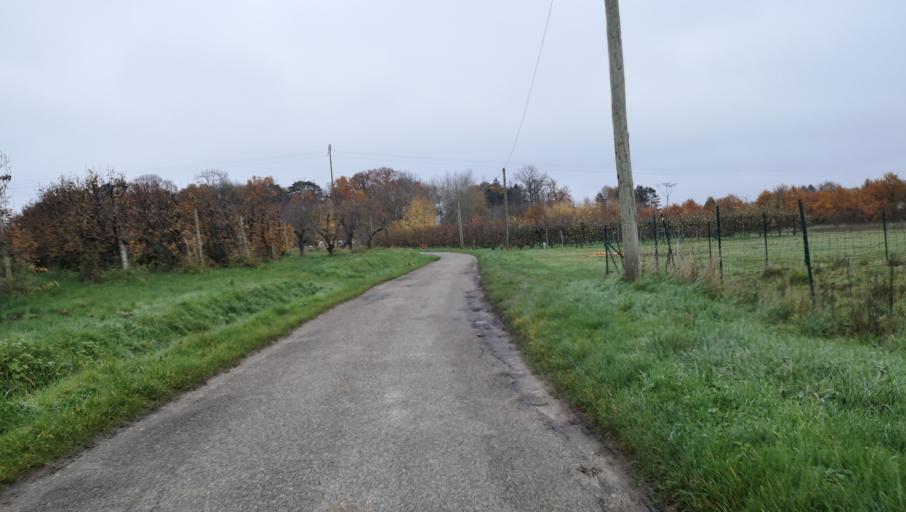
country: FR
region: Centre
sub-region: Departement du Loiret
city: Saint-Jean-de-Braye
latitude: 47.9284
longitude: 1.9773
